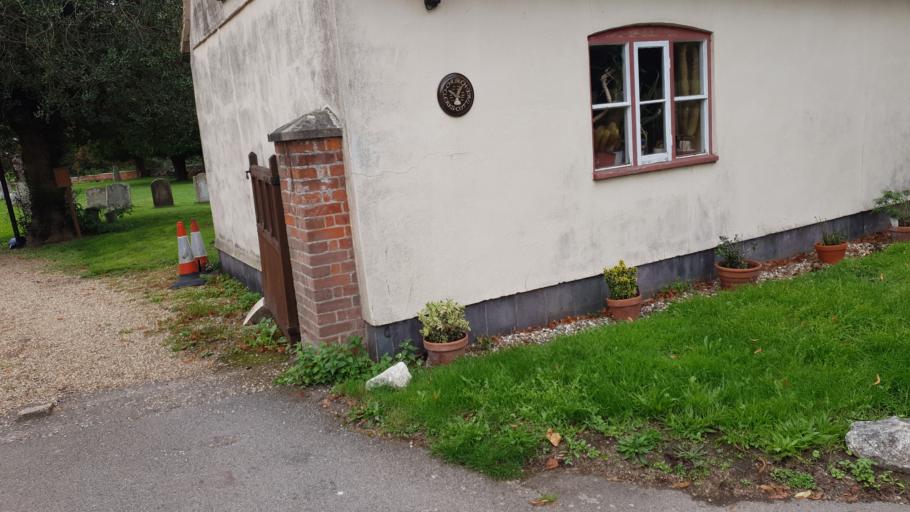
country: GB
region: England
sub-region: Essex
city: Manningtree
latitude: 51.9432
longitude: 1.0372
